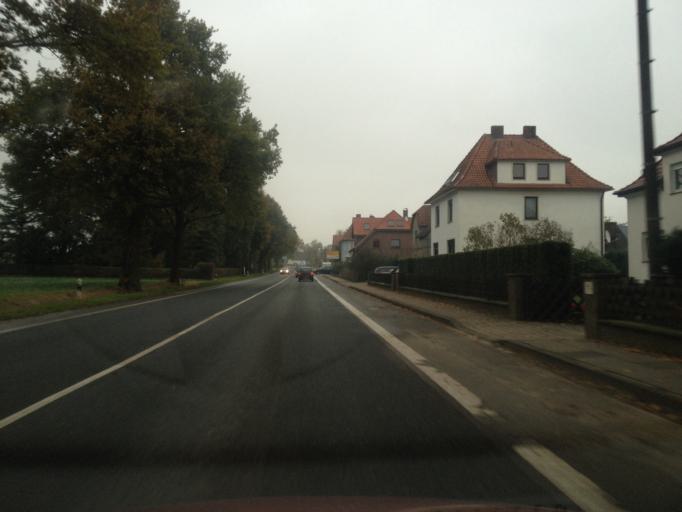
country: DE
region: North Rhine-Westphalia
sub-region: Regierungsbezirk Detmold
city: Bielefeld
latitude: 52.0711
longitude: 8.5781
